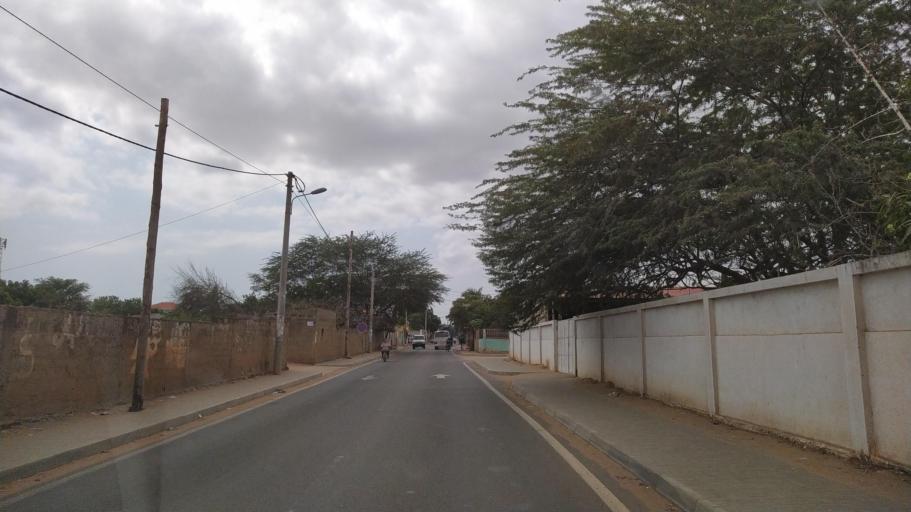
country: AO
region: Luanda
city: Luanda
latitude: -8.9667
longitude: 13.1527
